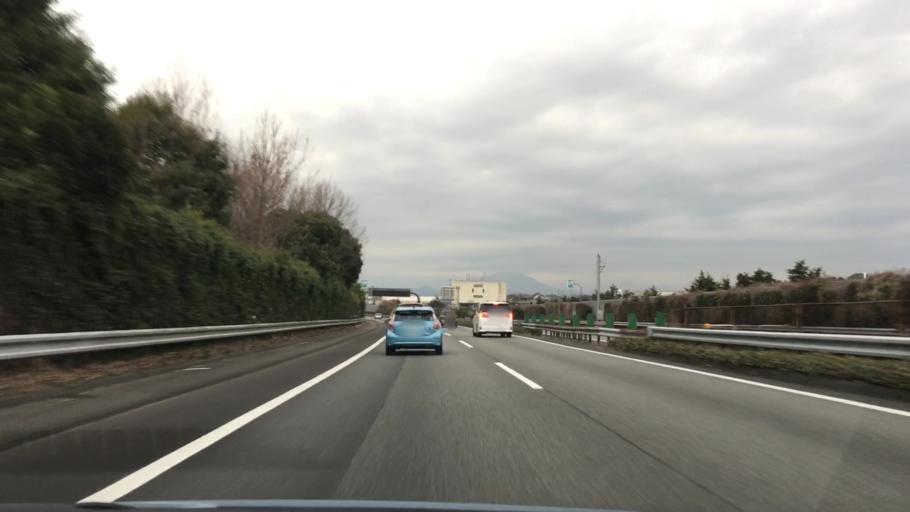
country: JP
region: Shizuoka
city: Fuji
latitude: 35.1801
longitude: 138.6857
